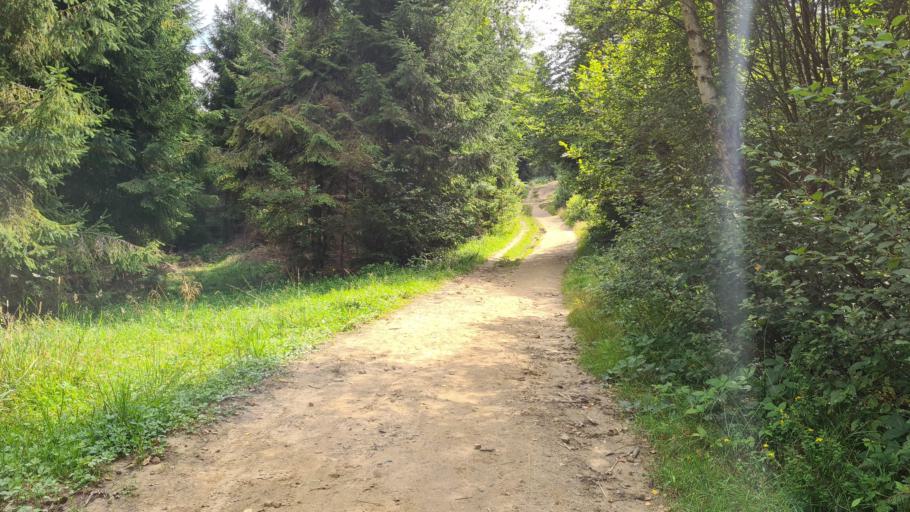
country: PL
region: Lesser Poland Voivodeship
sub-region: Powiat nowosadecki
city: Piwniczna-Zdroj
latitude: 49.4069
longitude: 20.6401
